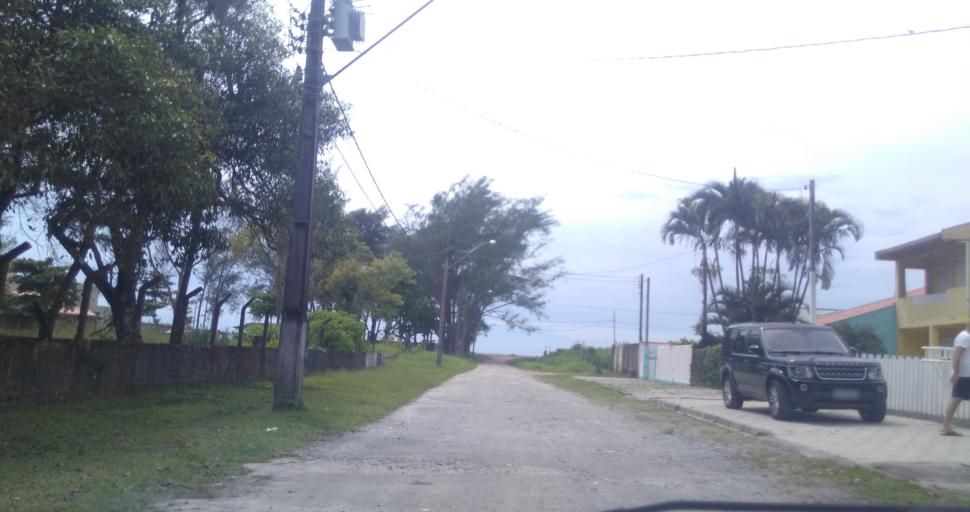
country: BR
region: Parana
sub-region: Pontal Do Parana
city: Pontal do Parana
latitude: -25.7664
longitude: -48.5110
